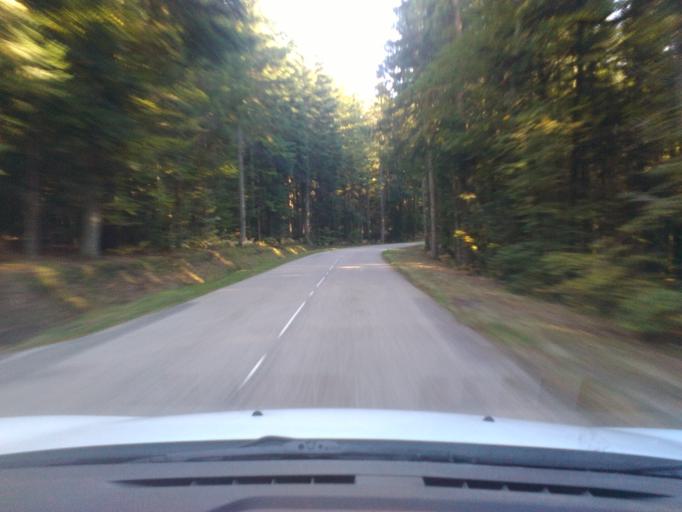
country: FR
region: Lorraine
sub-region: Departement des Vosges
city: Etival-Clairefontaine
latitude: 48.2907
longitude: 6.7853
